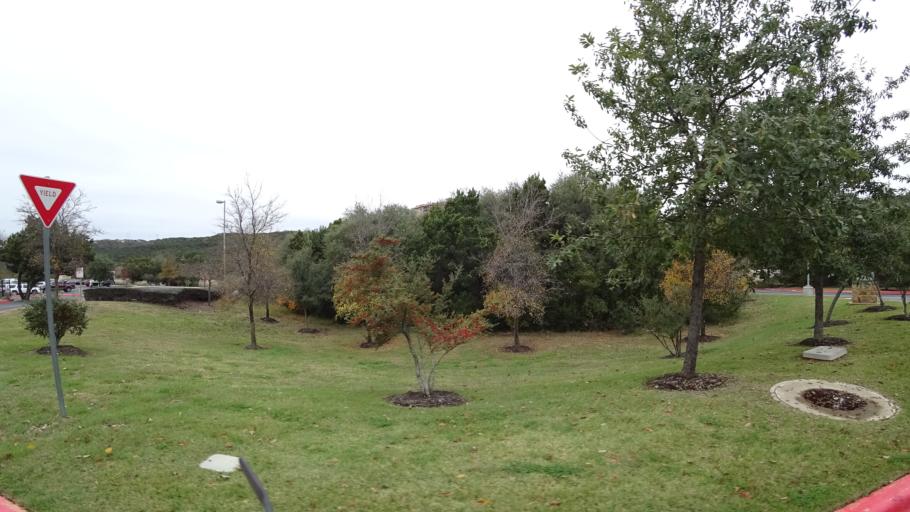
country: US
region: Texas
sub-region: Williamson County
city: Jollyville
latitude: 30.3734
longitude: -97.8030
